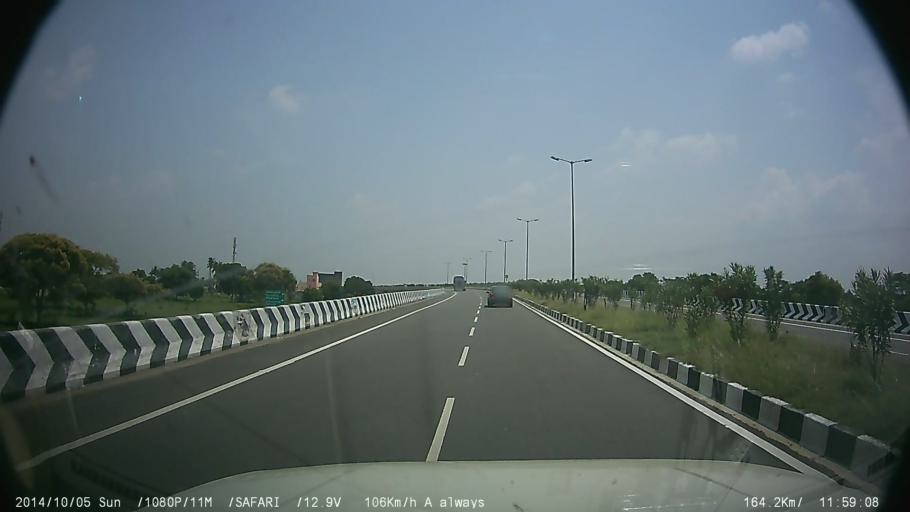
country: IN
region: Tamil Nadu
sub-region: Villupuram
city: Chinna Salem
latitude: 11.5927
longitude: 78.8041
